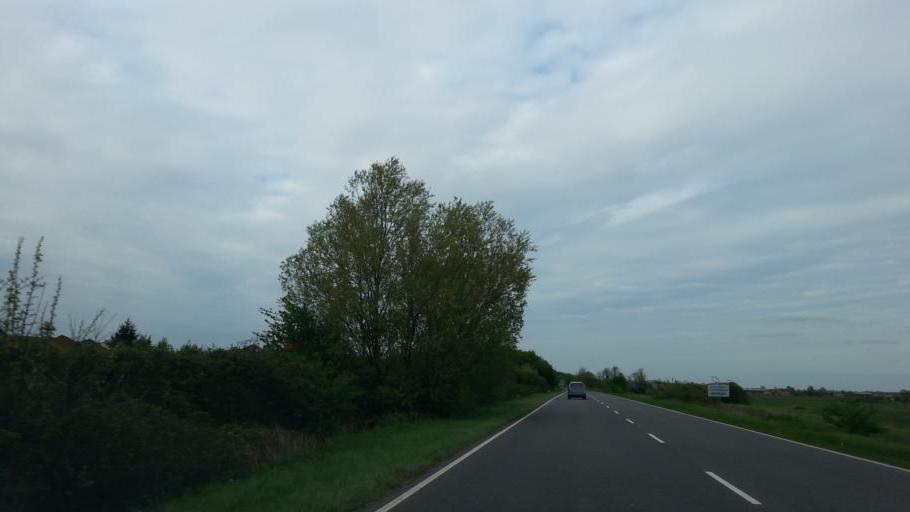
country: GB
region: England
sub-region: Cambridgeshire
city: Doddington
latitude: 52.5005
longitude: 0.0792
